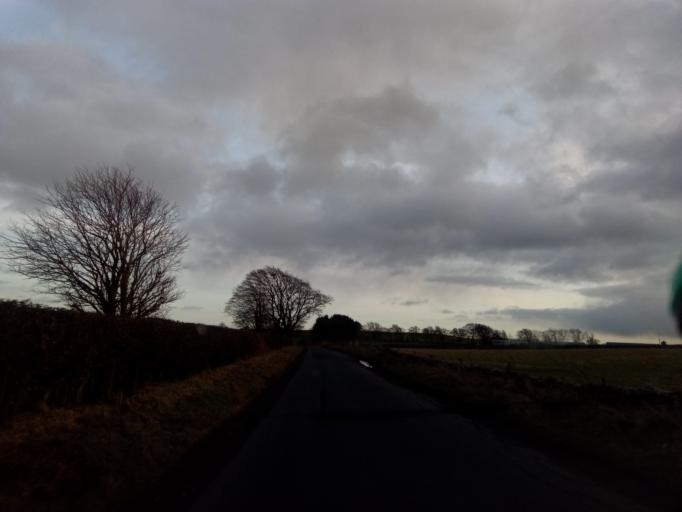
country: GB
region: Scotland
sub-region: The Scottish Borders
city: Selkirk
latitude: 55.5525
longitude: -2.7765
